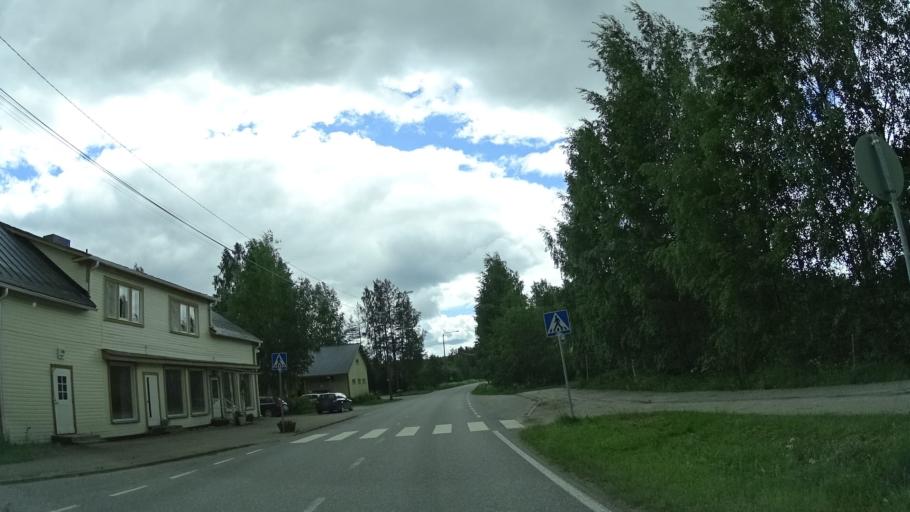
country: FI
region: Central Finland
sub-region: Jyvaeskylae
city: Toivakka
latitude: 61.9932
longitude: 25.9729
